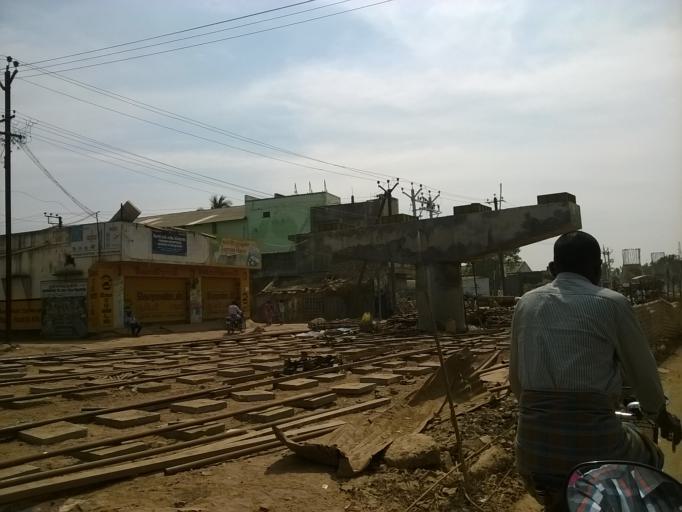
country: IN
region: Tamil Nadu
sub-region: Cuddalore
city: Panruti
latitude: 11.7773
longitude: 79.5534
